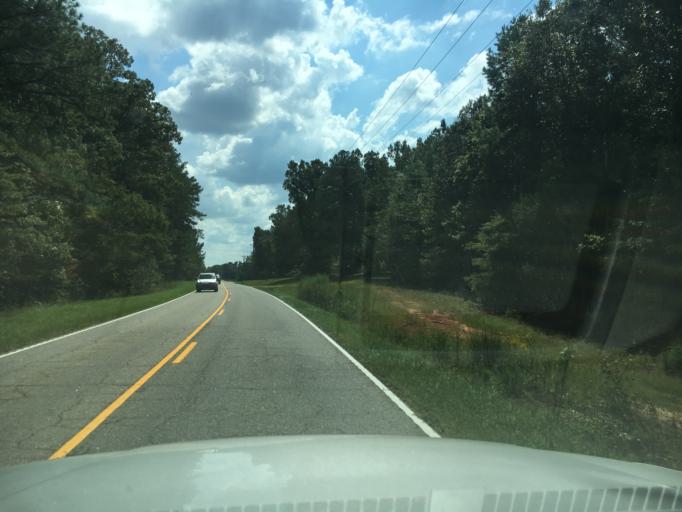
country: US
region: South Carolina
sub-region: Greenwood County
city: Greenwood
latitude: 34.0737
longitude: -82.1465
